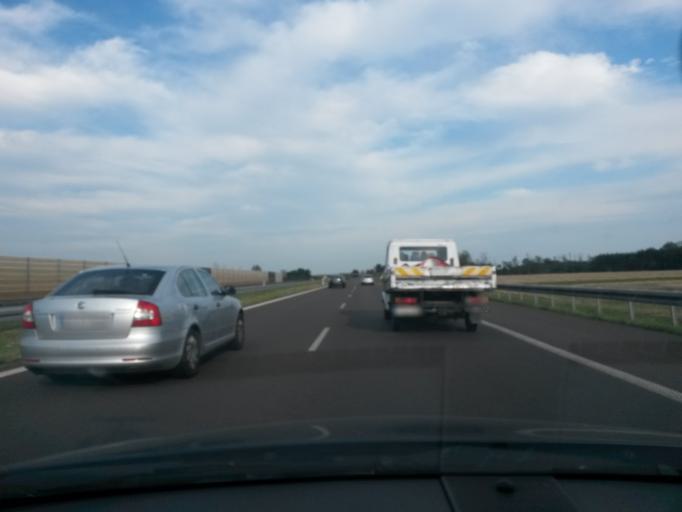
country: PL
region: Greater Poland Voivodeship
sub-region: Powiat turecki
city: Brudzew
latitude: 52.1320
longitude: 18.6457
